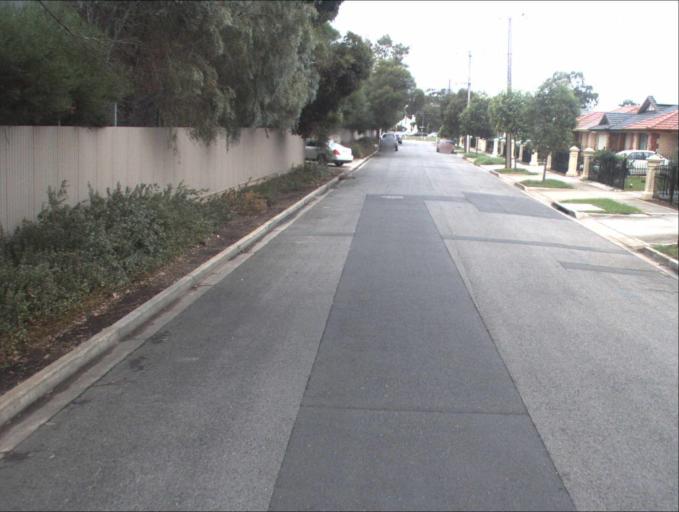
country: AU
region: South Australia
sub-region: Charles Sturt
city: Woodville North
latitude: -34.8542
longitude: 138.5611
